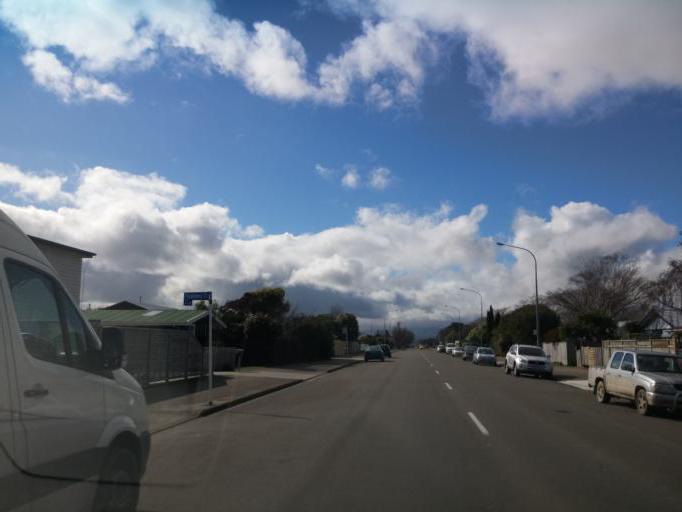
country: NZ
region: Manawatu-Wanganui
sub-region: Palmerston North City
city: Palmerston North
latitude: -40.3657
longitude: 175.5994
